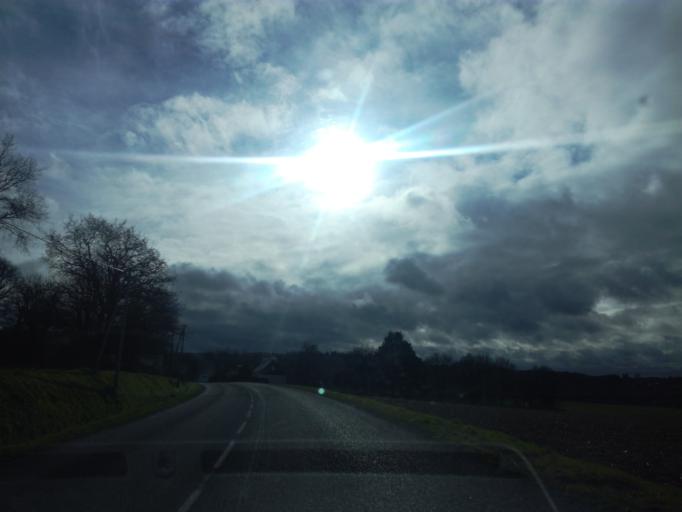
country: FR
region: Brittany
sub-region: Departement du Morbihan
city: Saint-Thuriau
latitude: 48.0284
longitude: -2.9694
